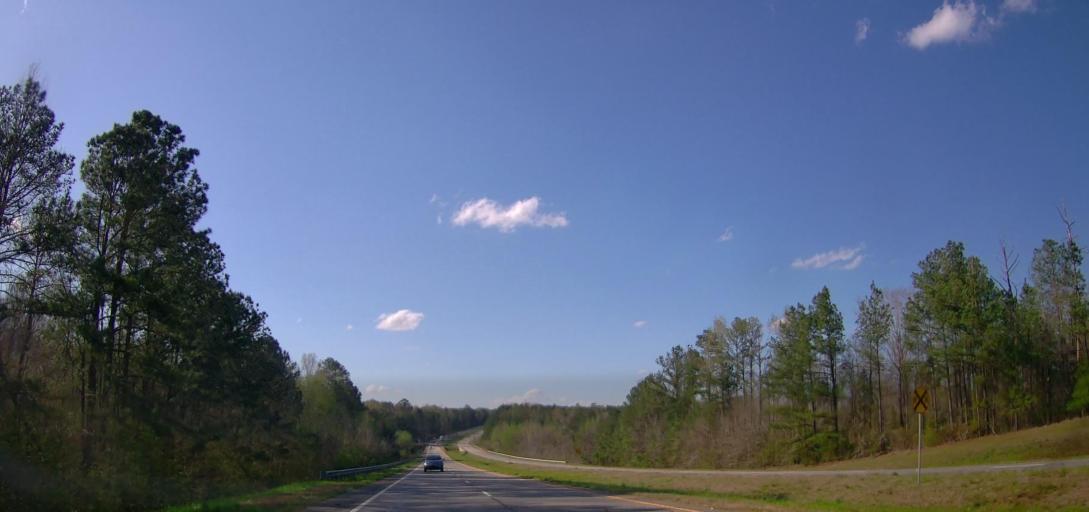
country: US
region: Georgia
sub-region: Baldwin County
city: Hardwick
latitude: 33.0312
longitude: -83.2480
